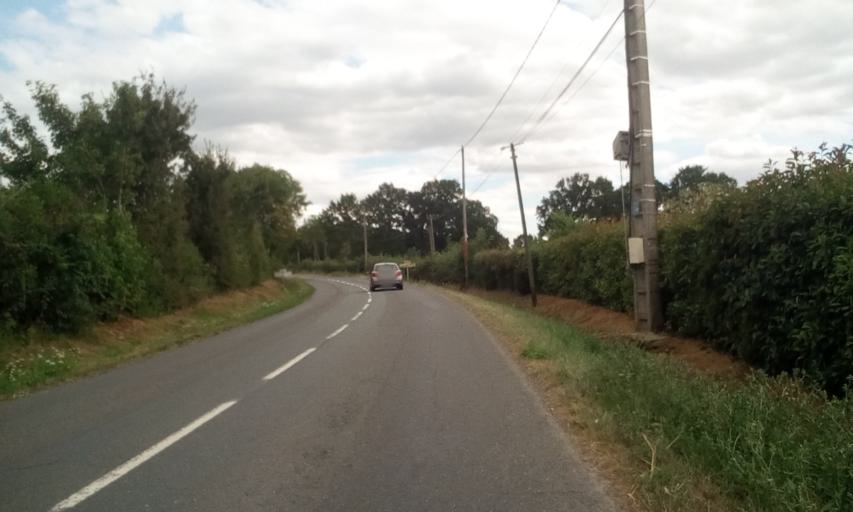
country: FR
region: Lower Normandy
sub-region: Departement du Calvados
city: Troarn
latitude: 49.1632
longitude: -0.1792
